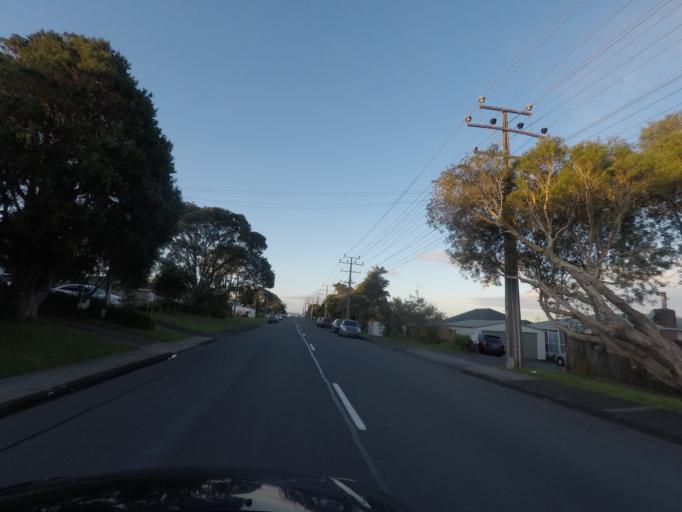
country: NZ
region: Auckland
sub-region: Auckland
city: Rosebank
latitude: -36.8919
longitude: 174.6548
